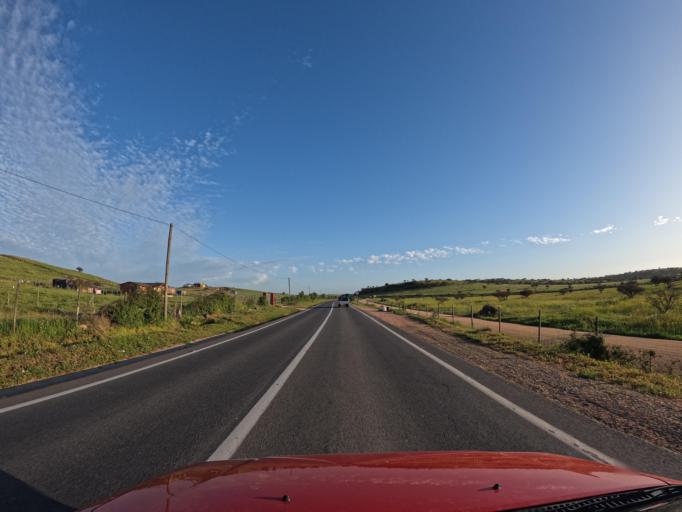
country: CL
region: O'Higgins
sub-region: Provincia de Colchagua
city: Santa Cruz
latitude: -34.2030
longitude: -71.7361
